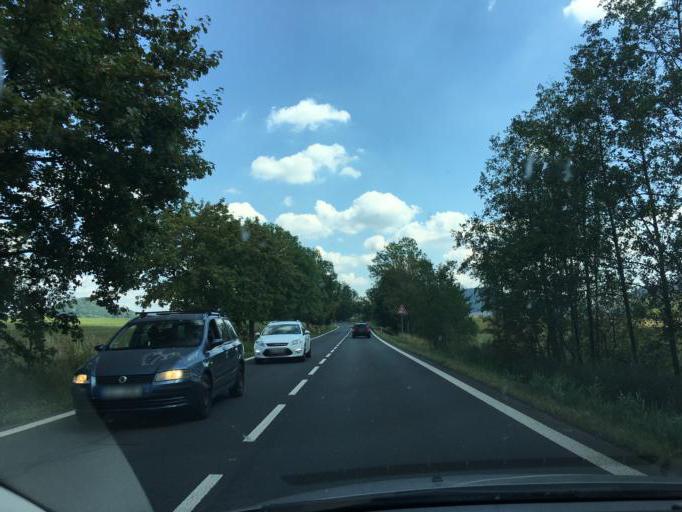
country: CZ
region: Ustecky
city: Benesov nad Ploucnici
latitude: 50.7856
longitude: 14.3463
